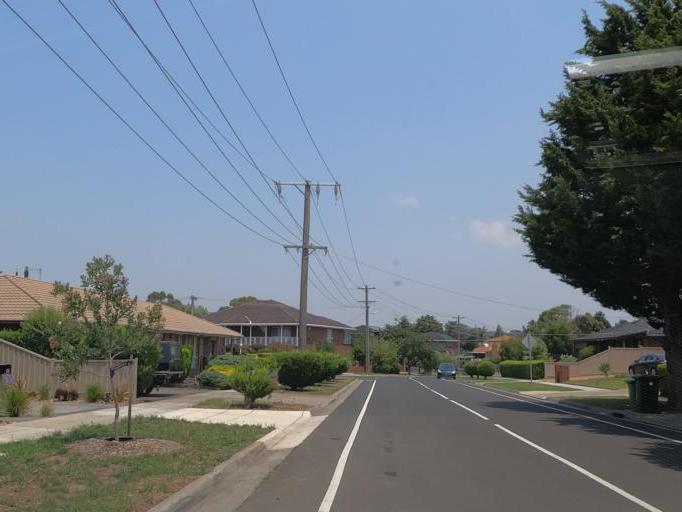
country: AU
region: Victoria
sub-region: Hume
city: Meadow Heights
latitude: -37.6434
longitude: 144.8964
